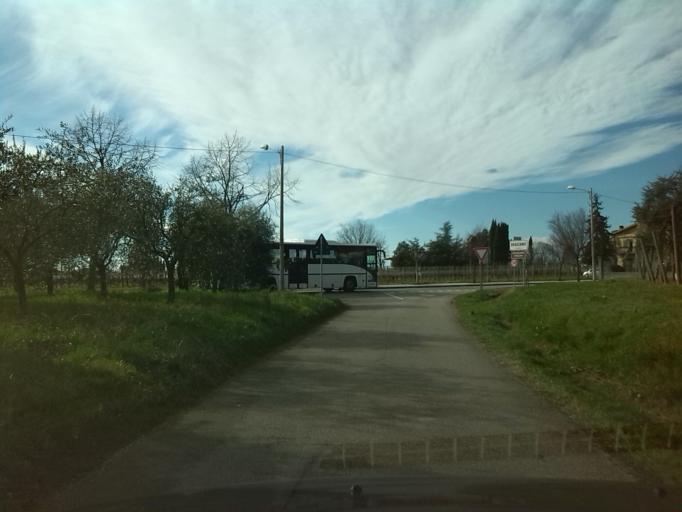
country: IT
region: Friuli Venezia Giulia
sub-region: Provincia di Gorizia
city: Cormons
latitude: 45.9710
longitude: 13.4575
